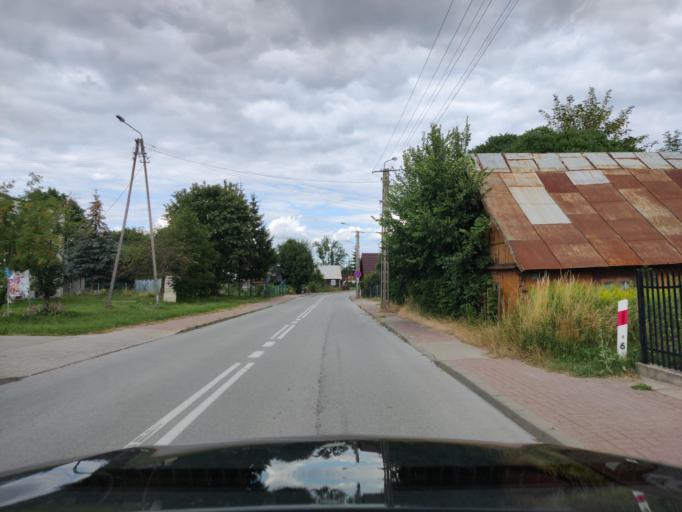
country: PL
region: Masovian Voivodeship
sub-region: Powiat sokolowski
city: Ceranow
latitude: 52.6281
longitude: 22.2242
